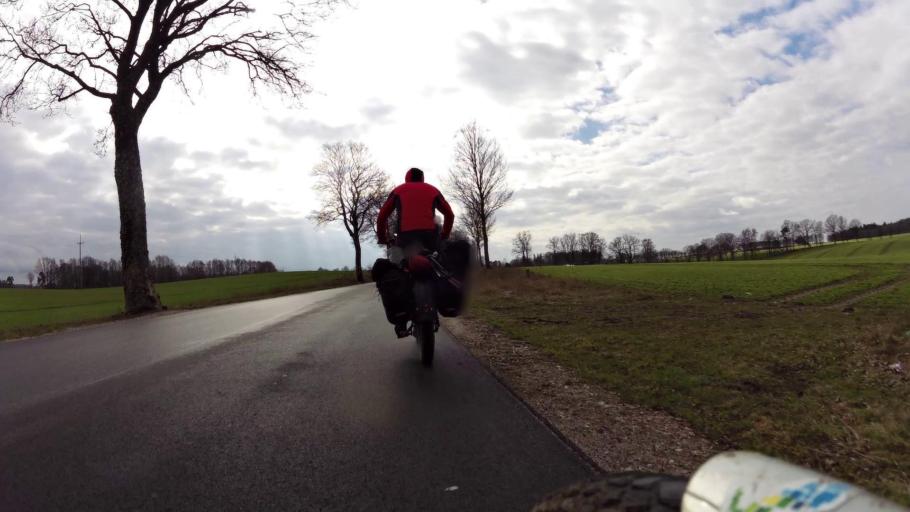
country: PL
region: Pomeranian Voivodeship
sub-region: Powiat bytowski
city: Kolczyglowy
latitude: 54.2262
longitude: 17.2416
